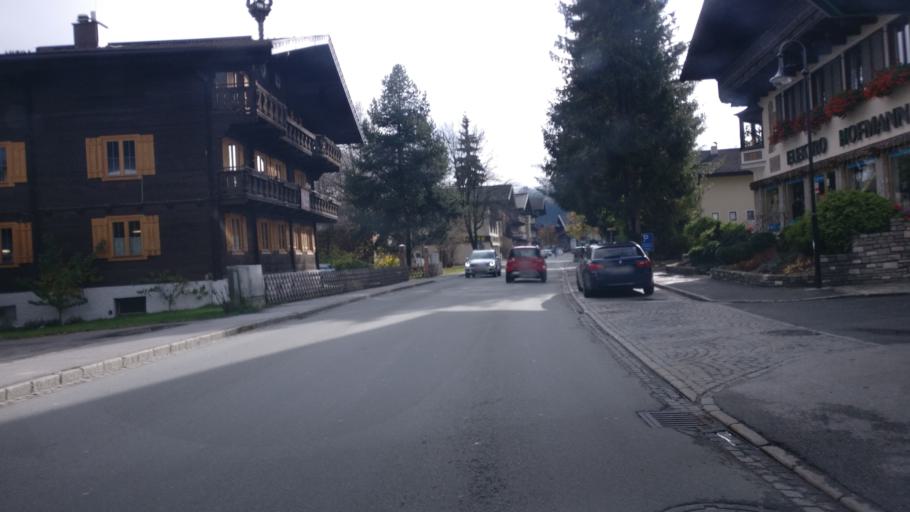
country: AT
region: Salzburg
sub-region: Politischer Bezirk Sankt Johann im Pongau
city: Altenmarkt im Pongau
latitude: 47.3809
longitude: 13.4182
